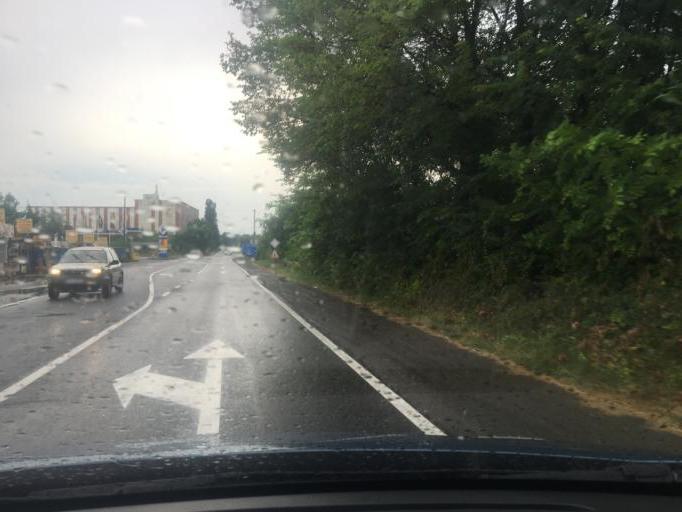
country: BG
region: Burgas
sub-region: Obshtina Pomorie
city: Pomorie
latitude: 42.5774
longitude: 27.6068
